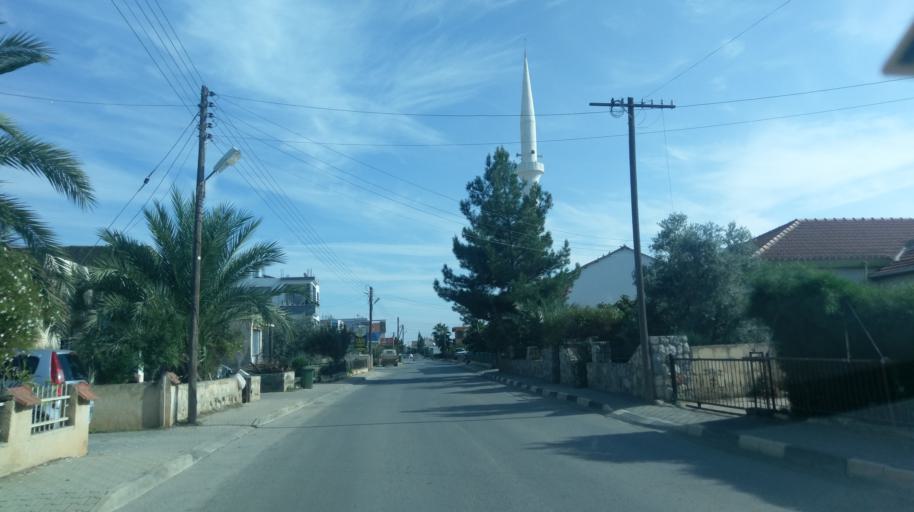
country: CY
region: Ammochostos
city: Trikomo
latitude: 35.1971
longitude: 33.8698
